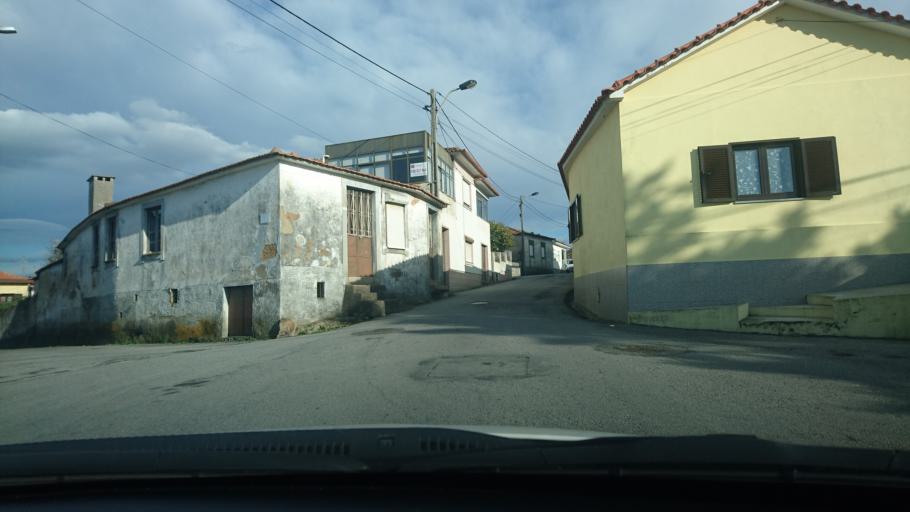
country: PT
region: Aveiro
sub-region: Ovar
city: Cortegaca
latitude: 40.9558
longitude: -8.6200
